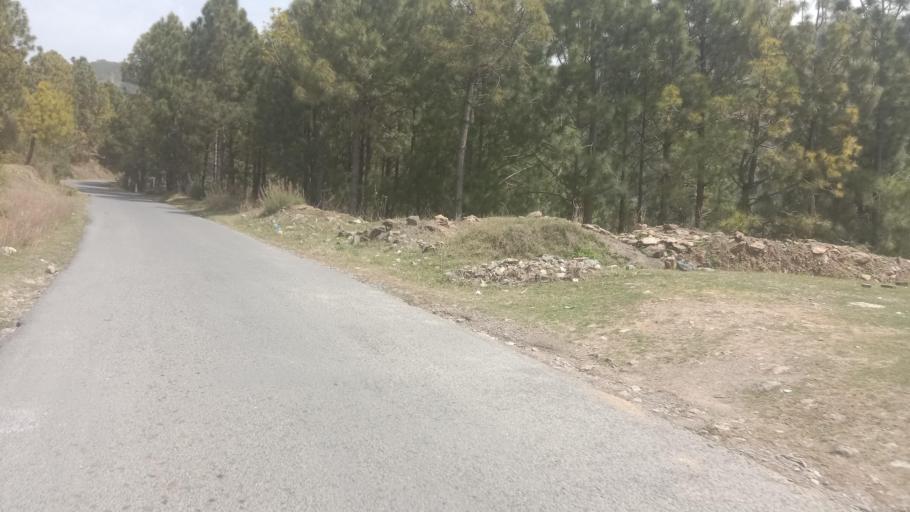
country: PK
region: Khyber Pakhtunkhwa
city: Abbottabad
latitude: 34.1670
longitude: 73.2851
